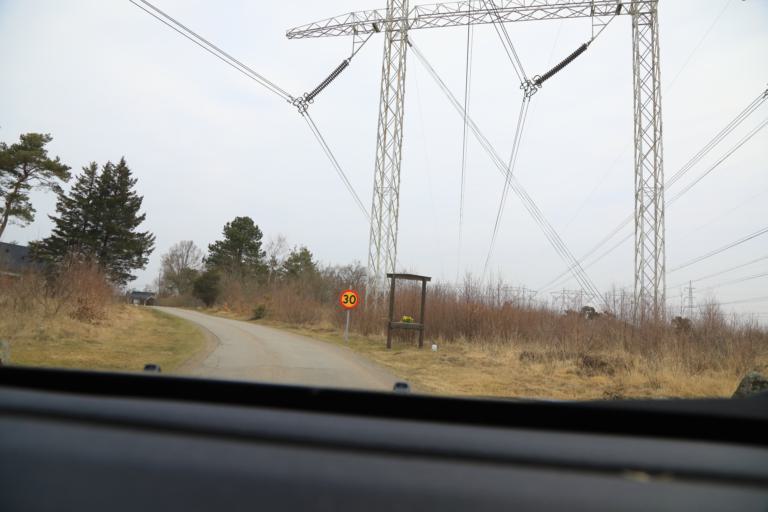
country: SE
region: Halland
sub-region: Kungsbacka Kommun
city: Frillesas
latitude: 57.2651
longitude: 12.1217
